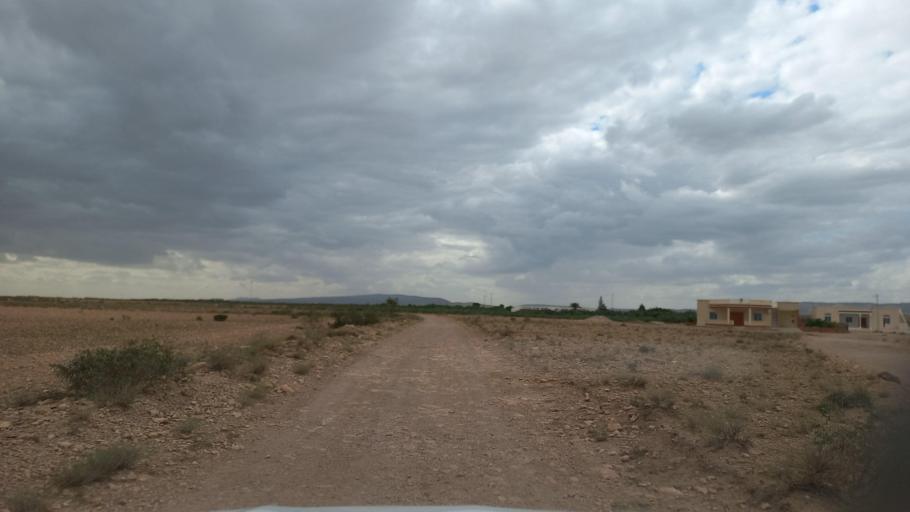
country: TN
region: Al Qasrayn
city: Sbiba
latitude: 35.3967
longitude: 9.1075
